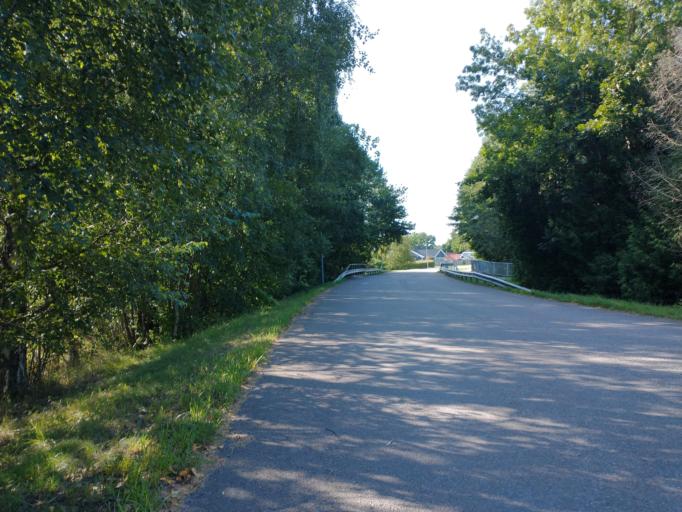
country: SE
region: Kalmar
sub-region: Kalmar Kommun
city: Lindsdal
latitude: 56.7824
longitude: 16.3024
